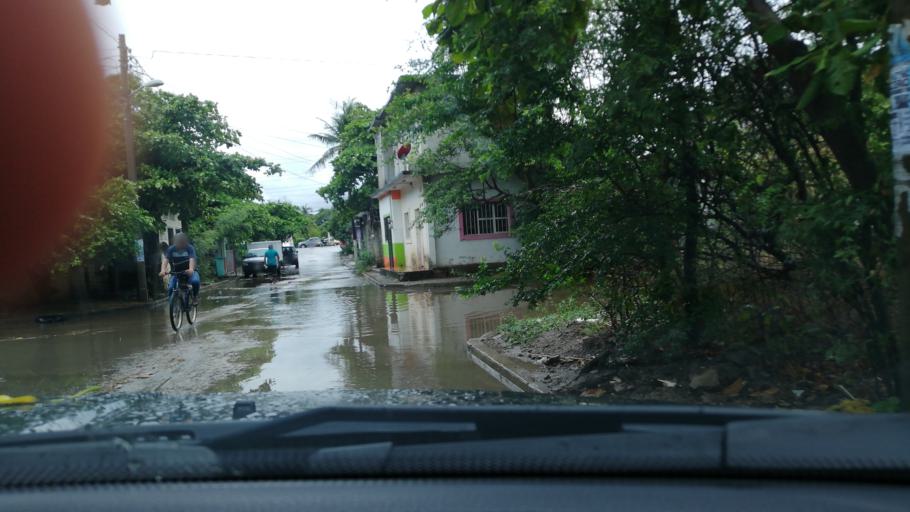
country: MX
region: Oaxaca
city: Juchitan de Zaragoza
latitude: 16.4483
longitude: -95.0188
